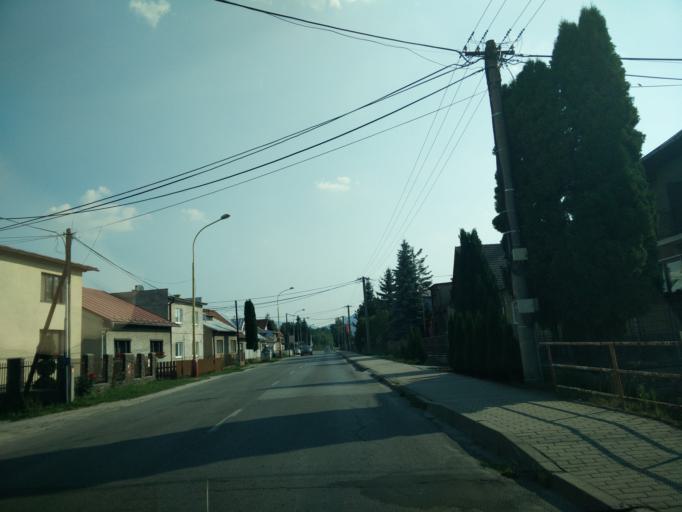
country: SK
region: Zilinsky
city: Rajec
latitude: 49.0798
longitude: 18.6320
